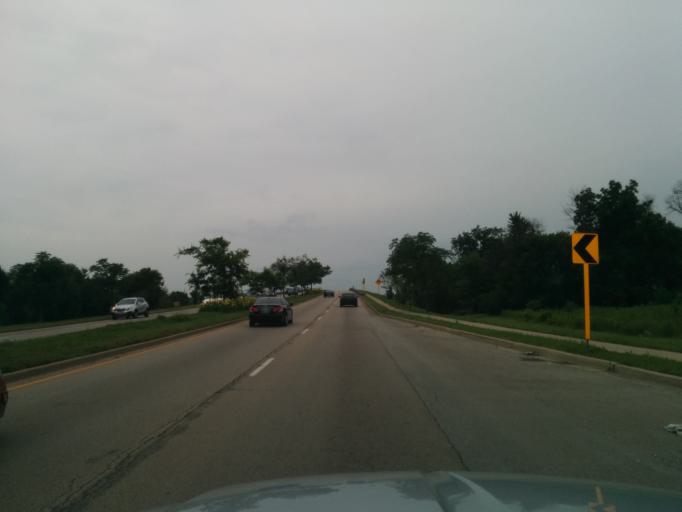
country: US
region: Illinois
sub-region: DuPage County
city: Warrenville
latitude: 41.7782
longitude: -88.2411
